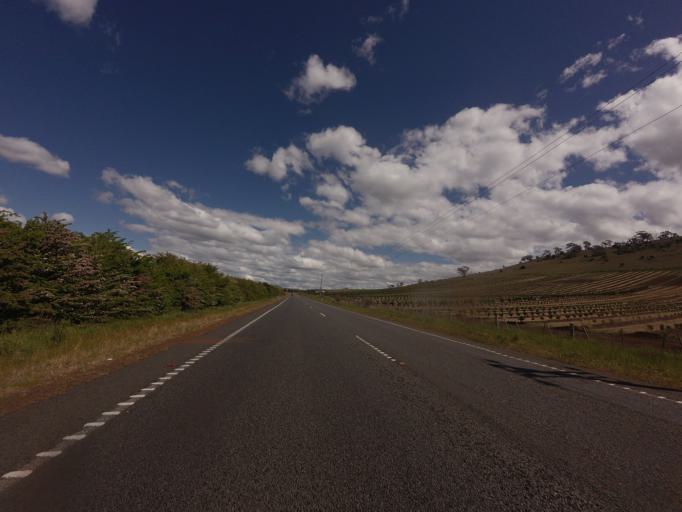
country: AU
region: Tasmania
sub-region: Northern Midlands
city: Evandale
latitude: -42.0529
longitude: 147.4823
